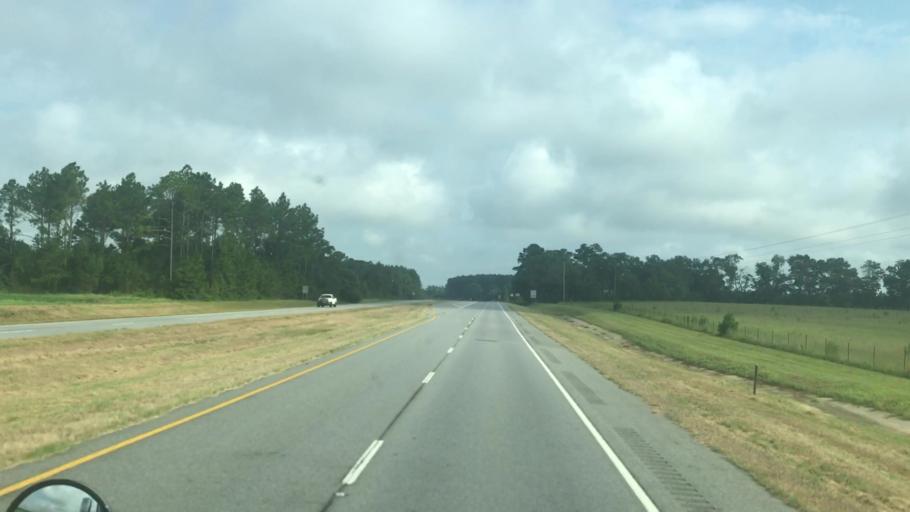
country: US
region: Georgia
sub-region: Miller County
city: Colquitt
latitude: 31.2212
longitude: -84.7792
